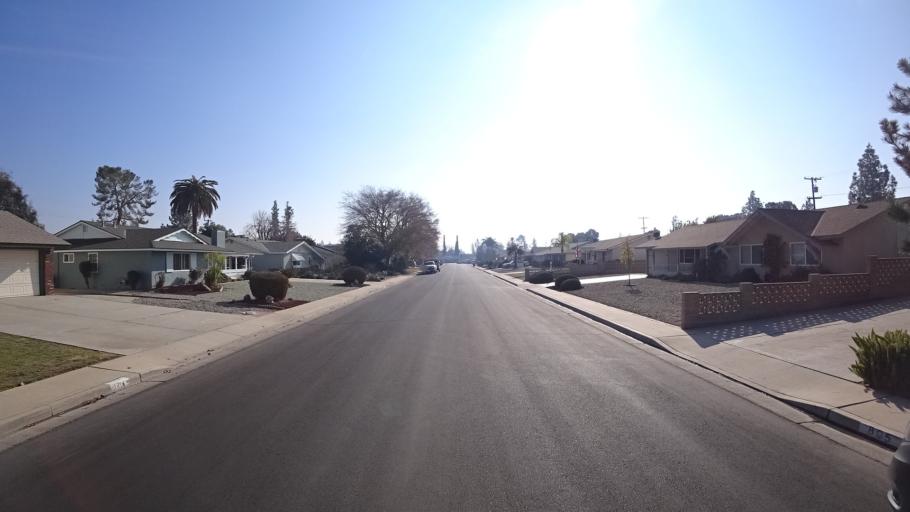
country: US
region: California
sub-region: Kern County
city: Bakersfield
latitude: 35.3475
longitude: -119.0646
